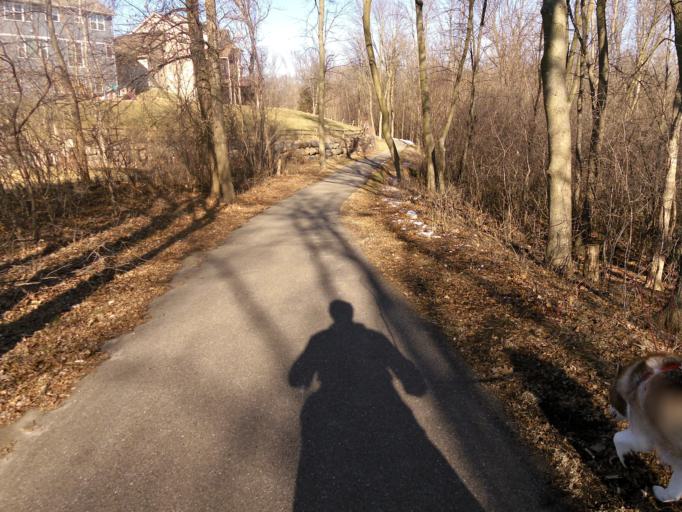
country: US
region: Minnesota
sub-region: Scott County
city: Prior Lake
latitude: 44.6986
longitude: -93.4411
